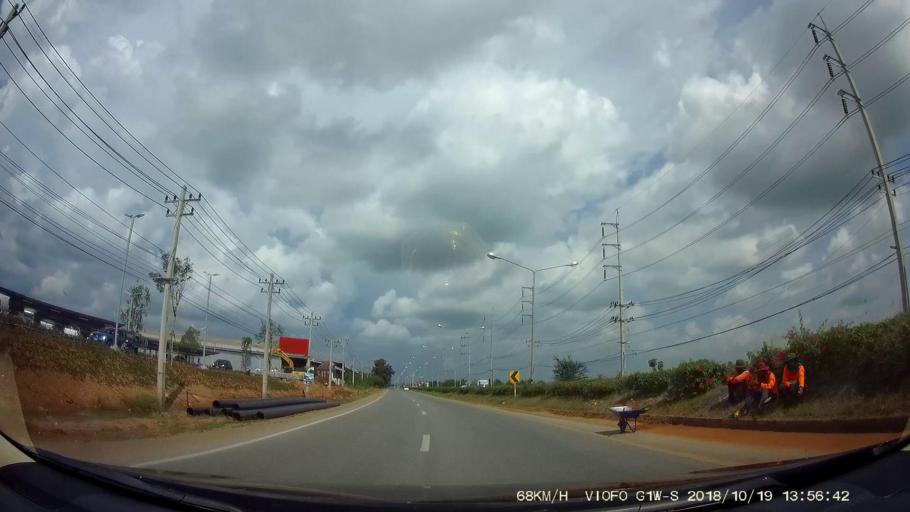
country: TH
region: Chaiyaphum
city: Chaiyaphum
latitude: 15.7861
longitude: 102.0323
